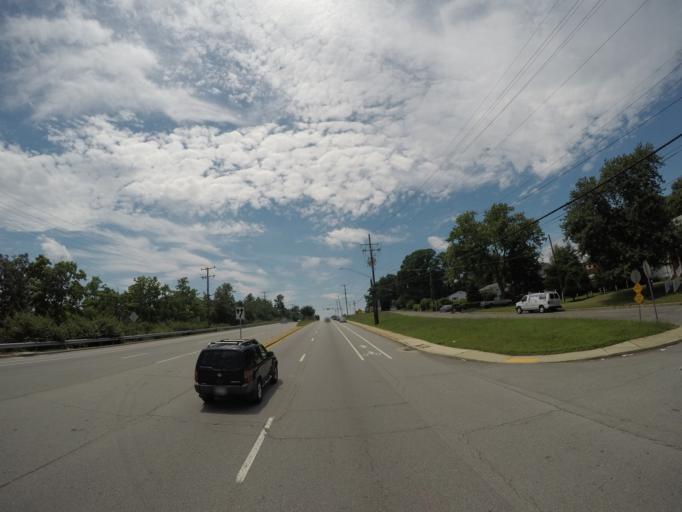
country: US
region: Maryland
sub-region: Prince George's County
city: Chillum
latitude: 38.9688
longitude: -76.9855
